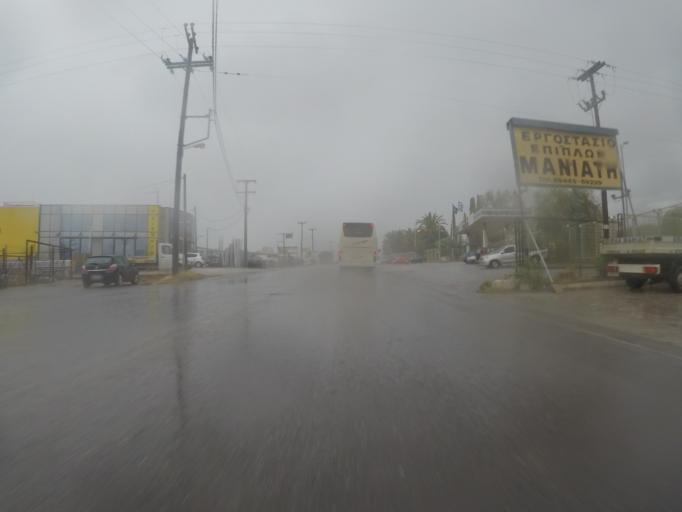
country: GR
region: Peloponnese
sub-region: Nomos Messinias
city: Sperkhoyia
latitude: 37.0461
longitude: 22.0815
